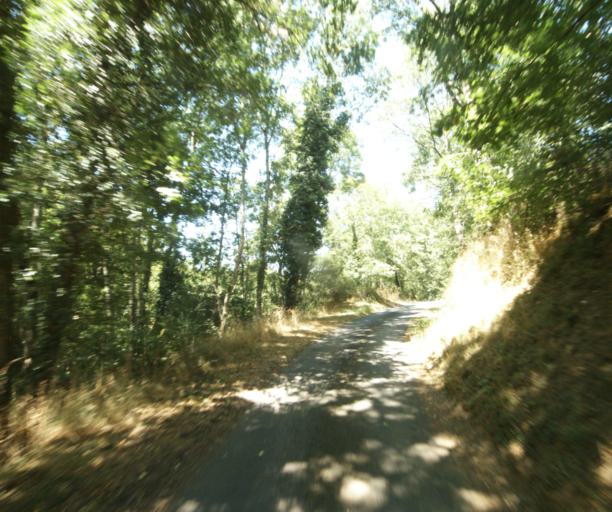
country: FR
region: Rhone-Alpes
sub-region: Departement du Rhone
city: Montrottier
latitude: 45.7895
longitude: 4.4995
